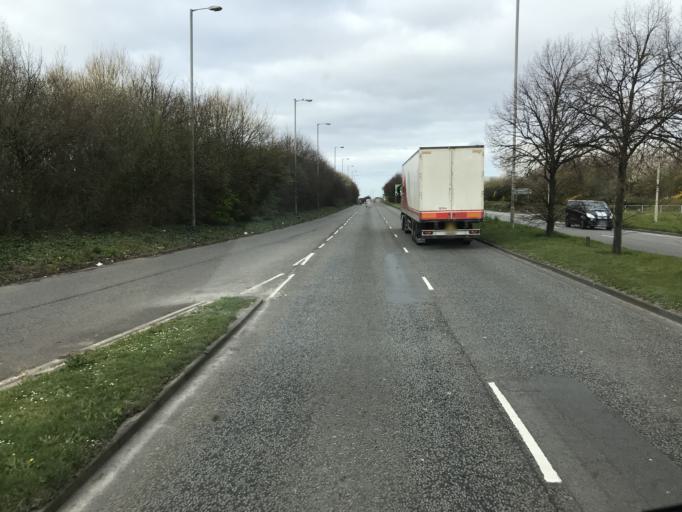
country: GB
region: England
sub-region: Borough of Halton
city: Hale
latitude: 53.3475
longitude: -2.8430
